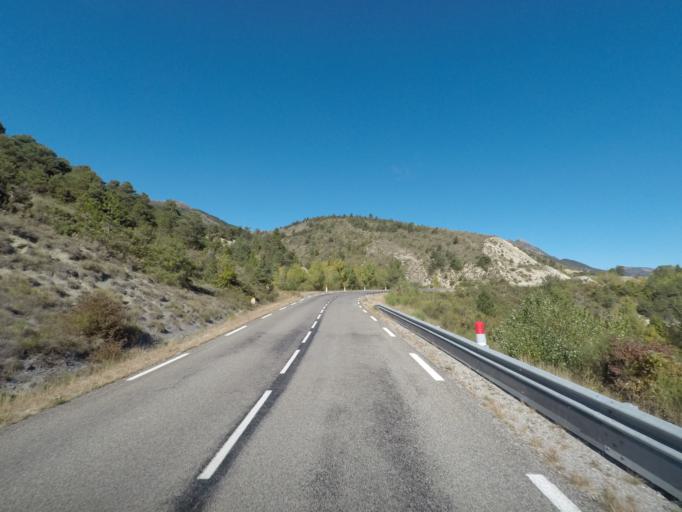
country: FR
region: Provence-Alpes-Cote d'Azur
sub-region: Departement des Hautes-Alpes
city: Serres
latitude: 44.3909
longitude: 5.4912
